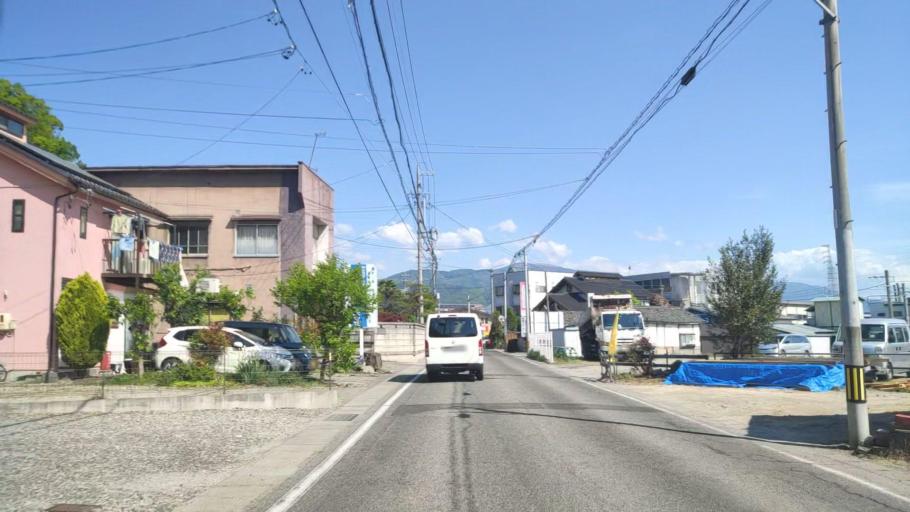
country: JP
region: Nagano
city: Matsumoto
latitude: 36.2422
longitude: 137.9551
